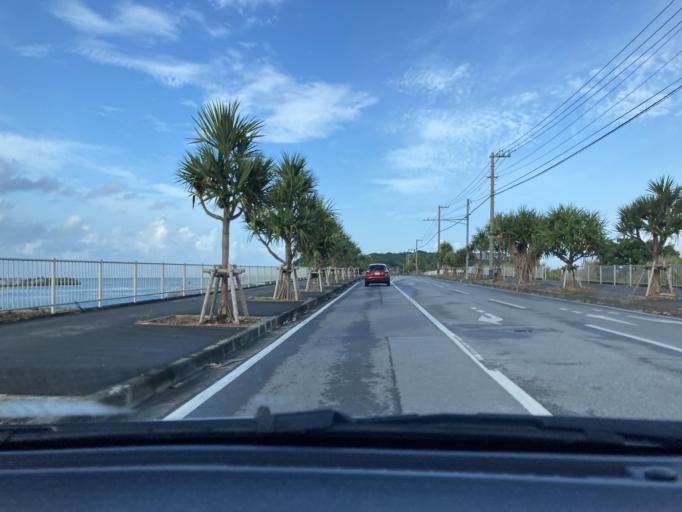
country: JP
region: Okinawa
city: Tomigusuku
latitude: 26.1753
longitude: 127.6508
